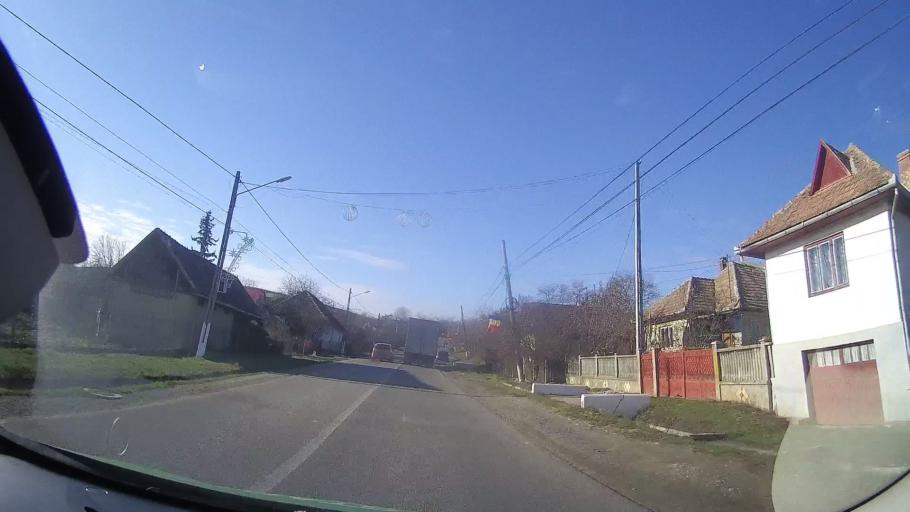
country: RO
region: Cluj
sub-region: Comuna Mociu
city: Mociu
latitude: 46.7966
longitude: 24.0218
